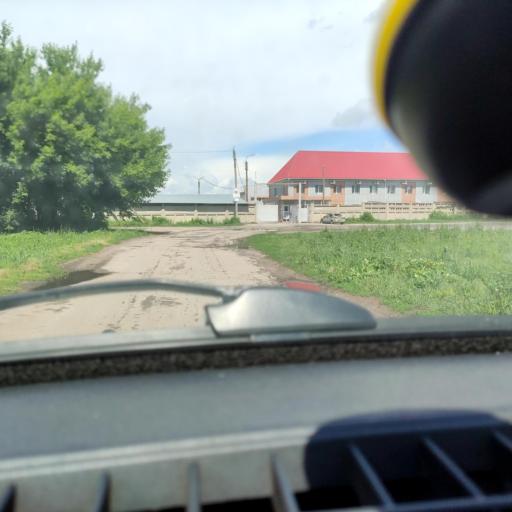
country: RU
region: Samara
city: Zhigulevsk
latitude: 53.5554
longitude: 49.5250
